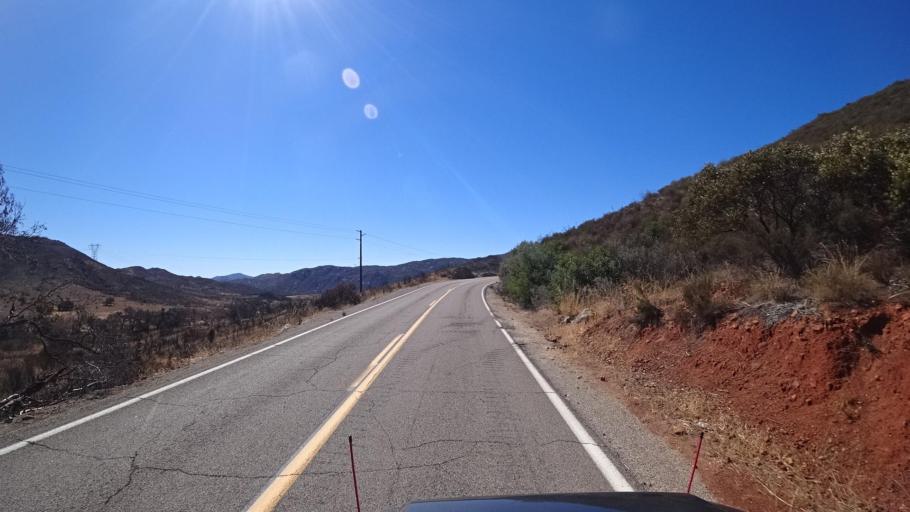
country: US
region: California
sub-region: San Diego County
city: Alpine
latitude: 32.7151
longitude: -116.7053
